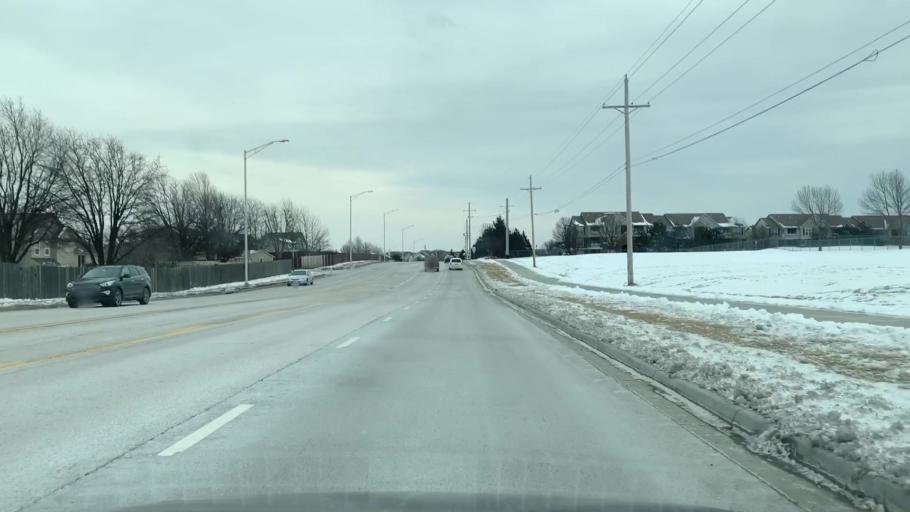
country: US
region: Missouri
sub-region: Jackson County
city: Lees Summit
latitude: 38.9304
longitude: -94.3723
